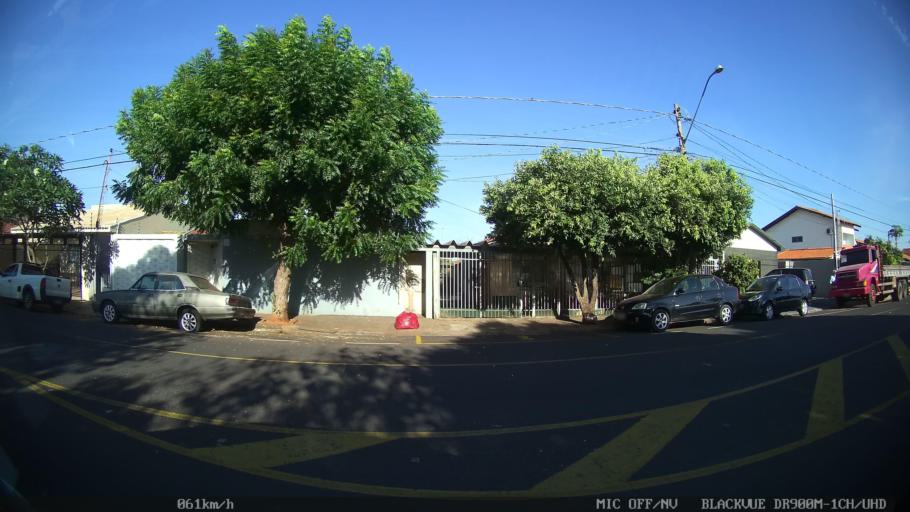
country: BR
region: Sao Paulo
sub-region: Sao Jose Do Rio Preto
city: Sao Jose do Rio Preto
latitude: -20.8195
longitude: -49.4080
